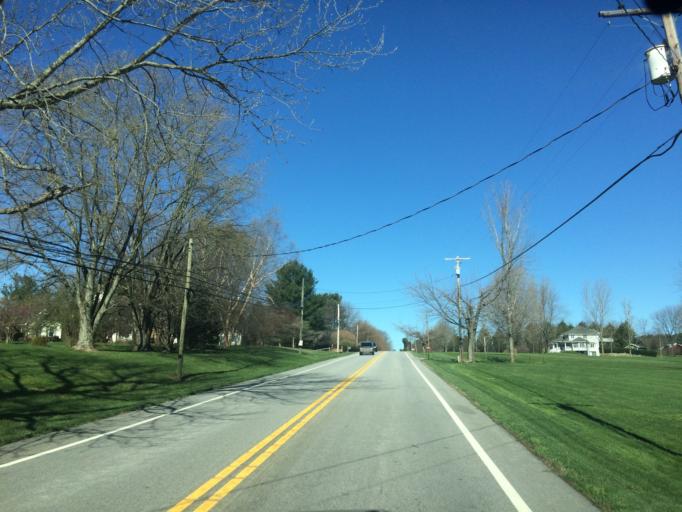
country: US
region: Maryland
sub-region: Carroll County
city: Mount Airy
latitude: 39.3392
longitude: -77.0810
